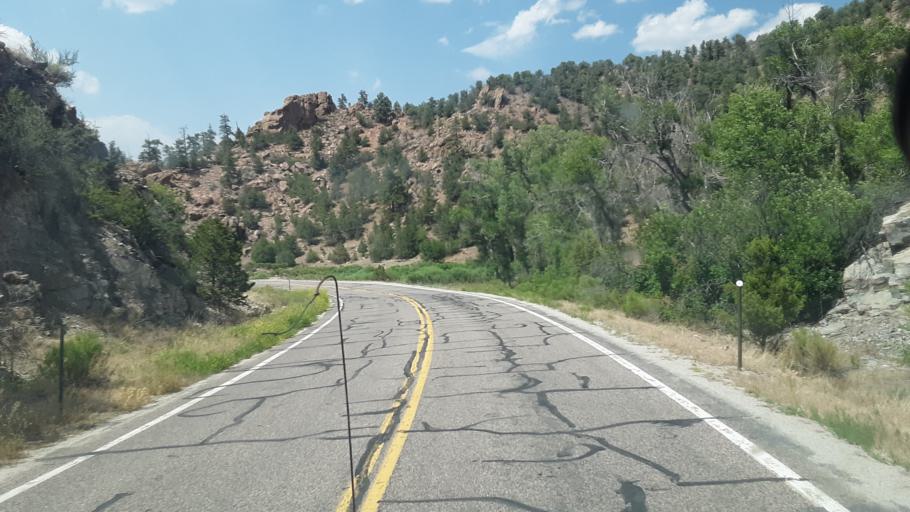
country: US
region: Colorado
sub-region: Custer County
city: Westcliffe
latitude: 38.3259
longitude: -105.6011
